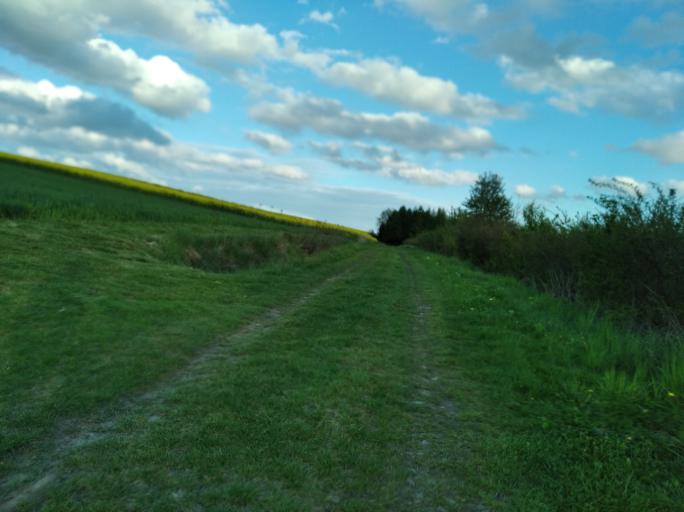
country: PL
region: Subcarpathian Voivodeship
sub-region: Powiat strzyzowski
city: Wysoka Strzyzowska
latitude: 49.8603
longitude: 21.7561
